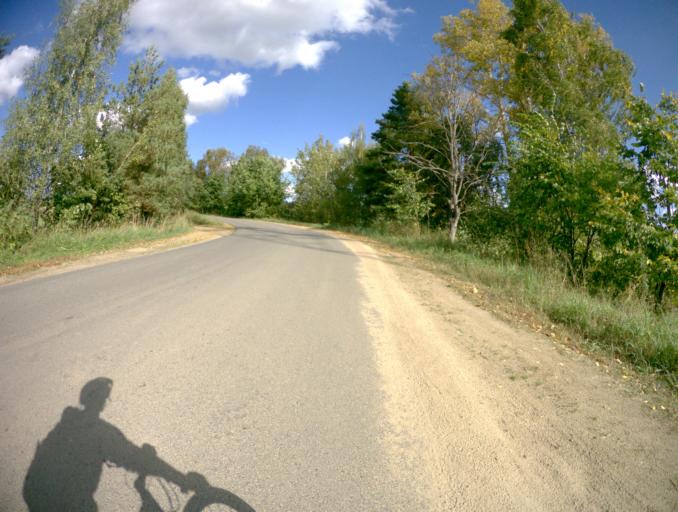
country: RU
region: Vladimir
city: Lakinsk
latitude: 55.9028
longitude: 39.8899
